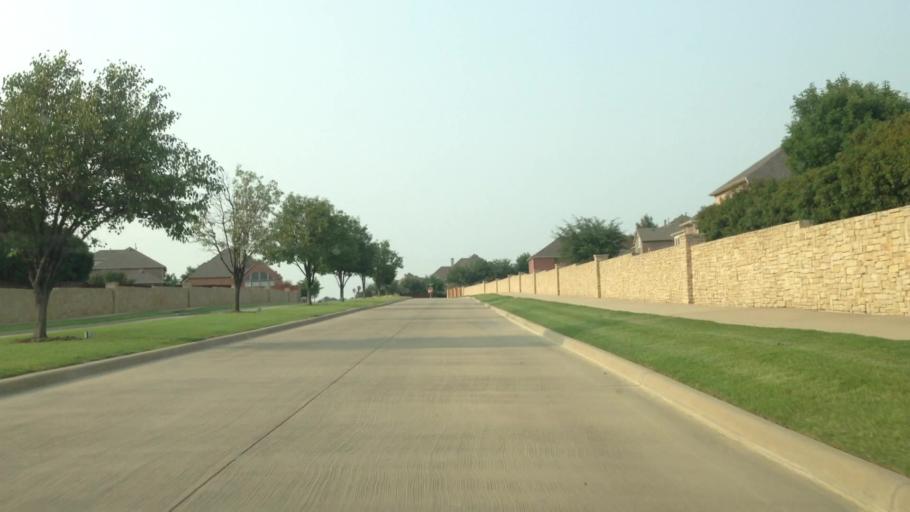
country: US
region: Texas
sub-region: Denton County
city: The Colony
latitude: 33.0379
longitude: -96.9147
